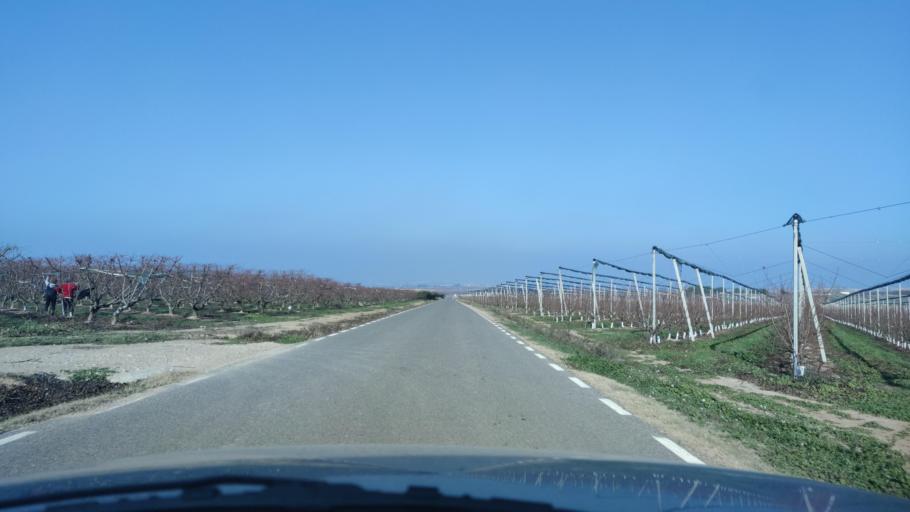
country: ES
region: Catalonia
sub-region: Provincia de Lleida
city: Sunyer
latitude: 41.5267
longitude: 0.5727
